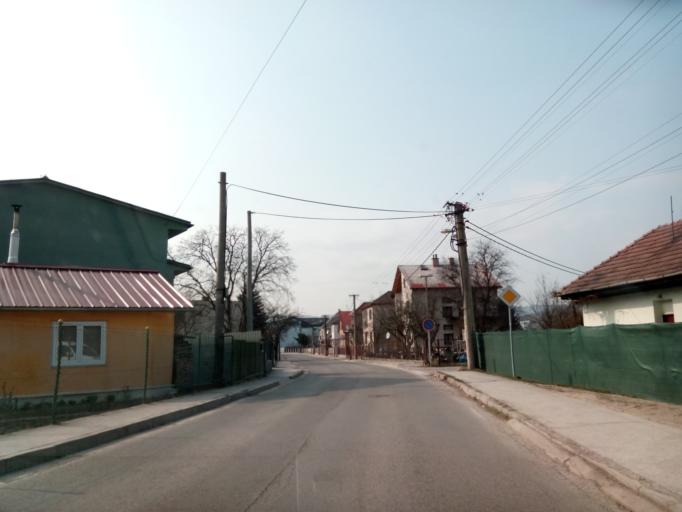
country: SK
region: Trenciansky
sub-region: Okres Trencin
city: Trencin
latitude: 48.9035
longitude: 18.0297
